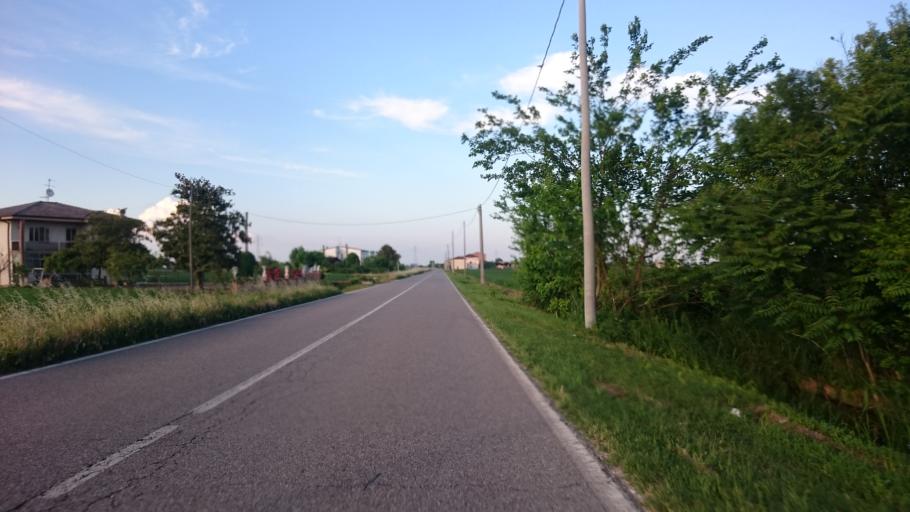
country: IT
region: Veneto
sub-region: Provincia di Verona
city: Casaleone
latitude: 45.1452
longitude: 11.1710
